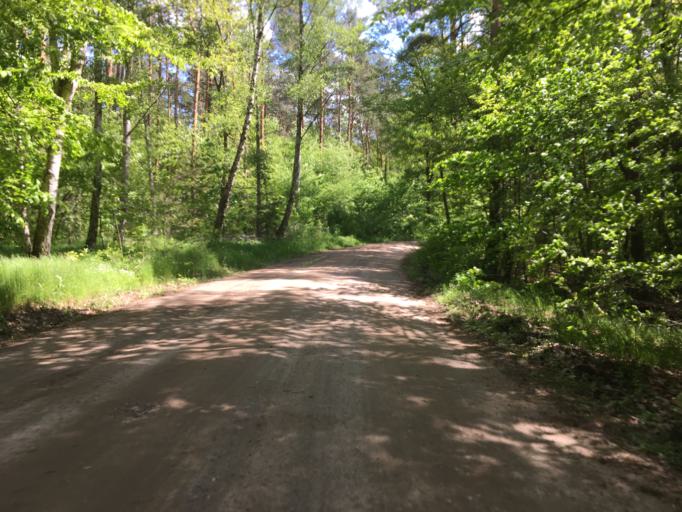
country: DE
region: Brandenburg
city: Friedrichswalde
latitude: 53.0067
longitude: 13.6328
